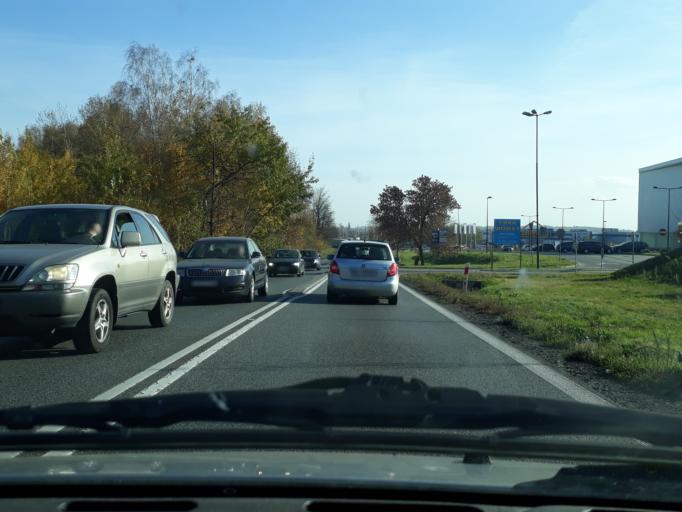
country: PL
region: Silesian Voivodeship
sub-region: Powiat tarnogorski
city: Tarnowskie Gory
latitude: 50.4394
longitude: 18.8387
